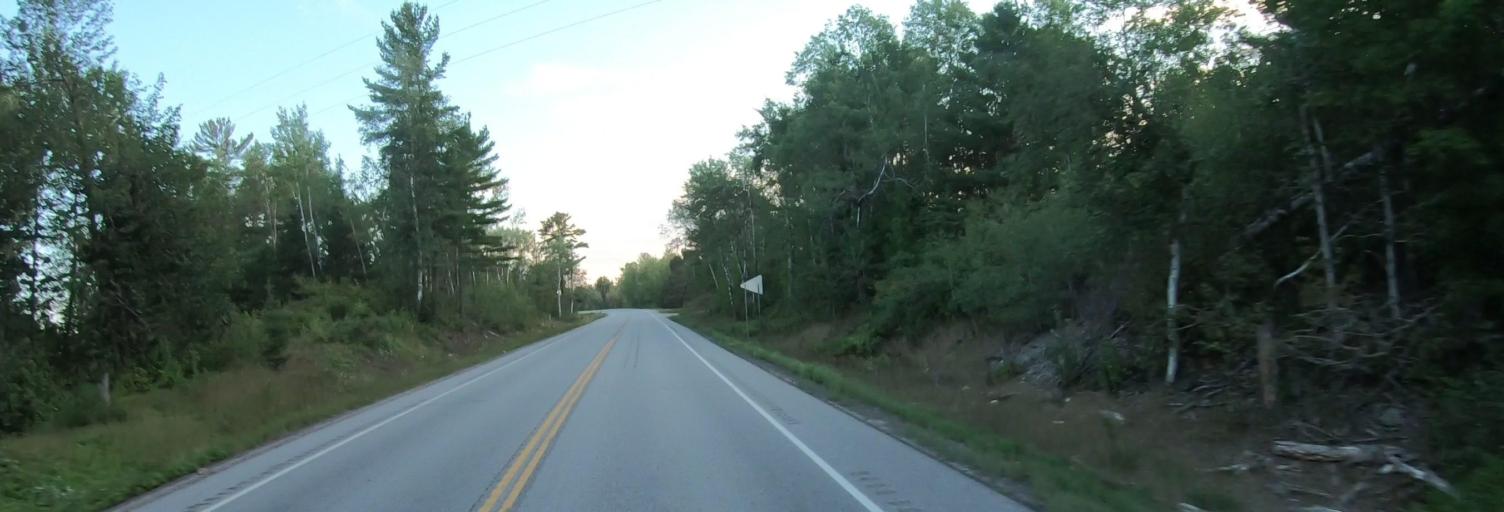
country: US
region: Minnesota
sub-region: Saint Louis County
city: Ely
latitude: 47.8607
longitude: -92.0397
